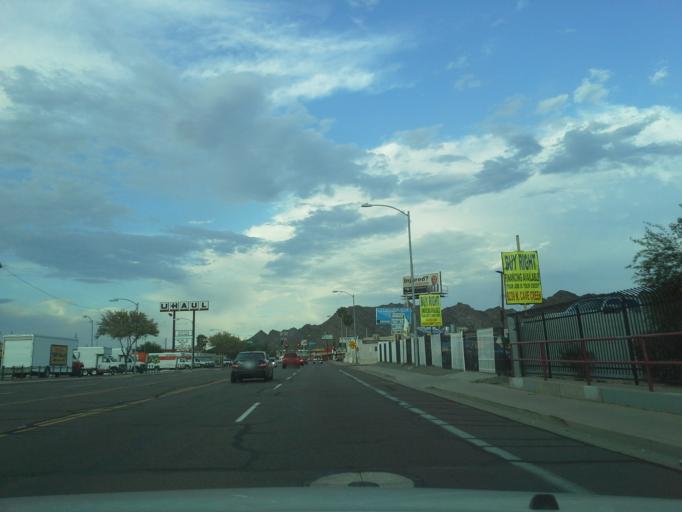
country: US
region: Arizona
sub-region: Maricopa County
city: Phoenix
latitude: 33.5700
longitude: -112.0623
